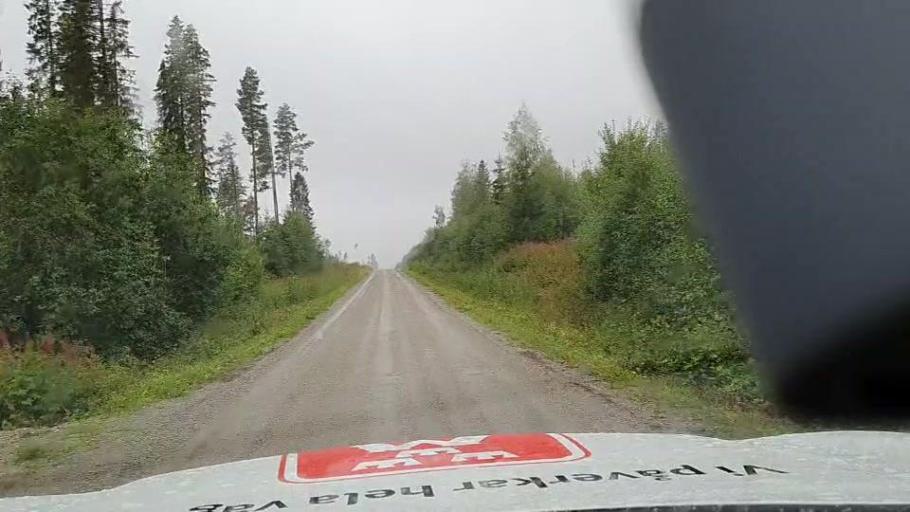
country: SE
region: Jaemtland
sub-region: OEstersunds Kommun
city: Brunflo
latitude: 62.8153
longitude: 15.0547
